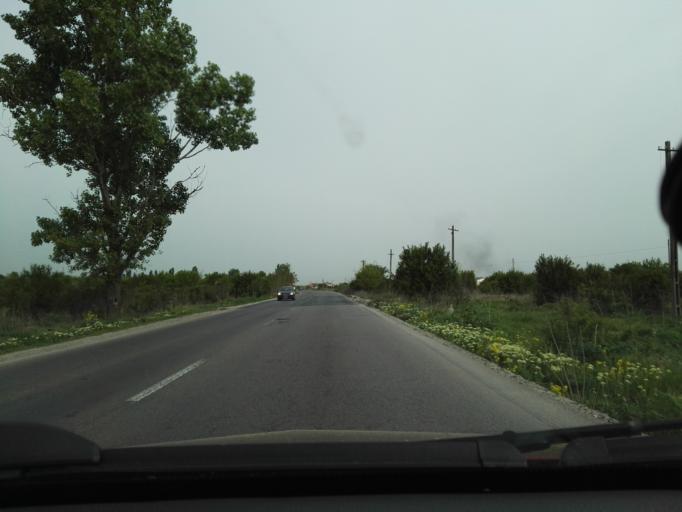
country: RO
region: Ilfov
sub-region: Comuna Magurele
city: Varteju
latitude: 44.3730
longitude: 26.0084
